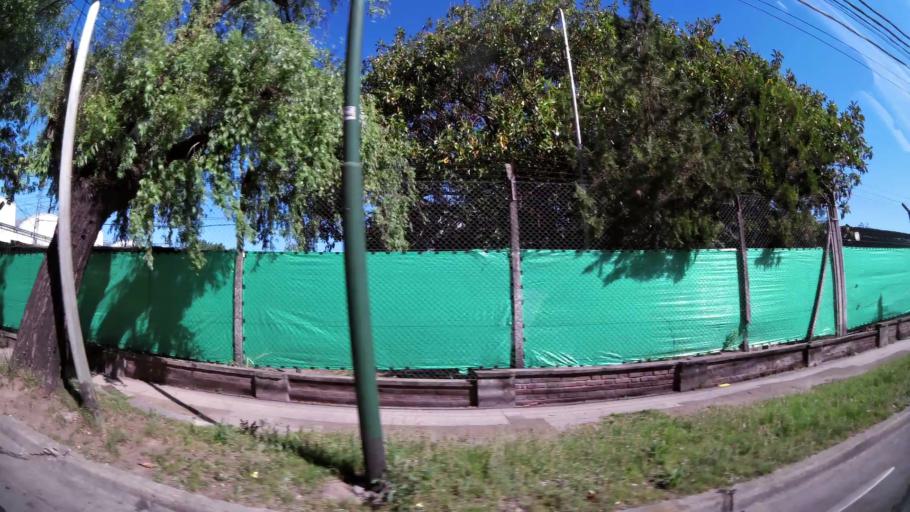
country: AR
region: Buenos Aires
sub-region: Partido de San Isidro
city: San Isidro
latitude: -34.4677
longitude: -58.5412
